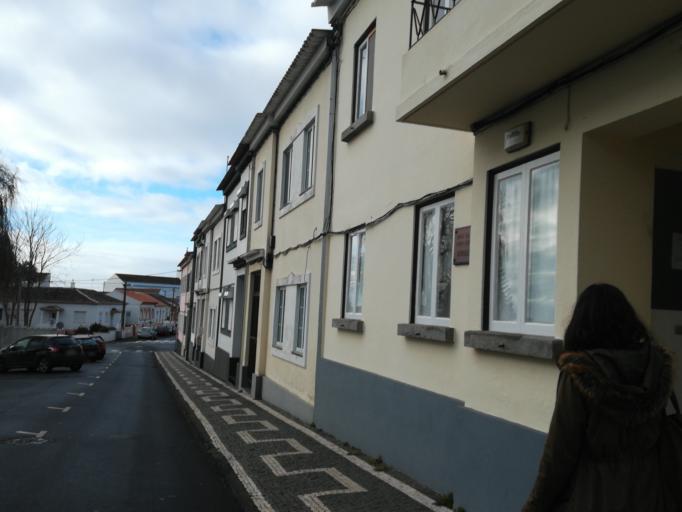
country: PT
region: Azores
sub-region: Angra do Heroismo
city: Angra do Heroismo
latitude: 38.6551
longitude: -27.2145
